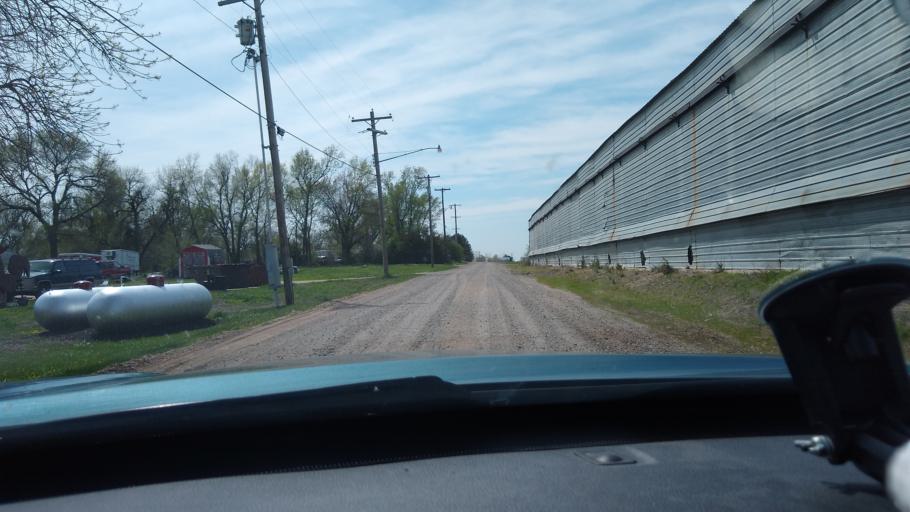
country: US
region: Nebraska
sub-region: Fillmore County
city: Geneva
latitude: 40.4155
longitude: -97.5870
